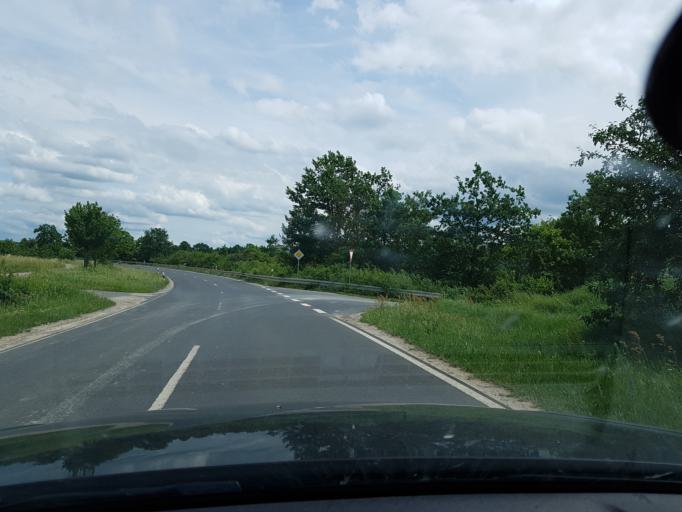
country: DE
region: Bavaria
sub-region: Regierungsbezirk Unterfranken
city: Nordheim
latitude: 49.8731
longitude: 10.1812
